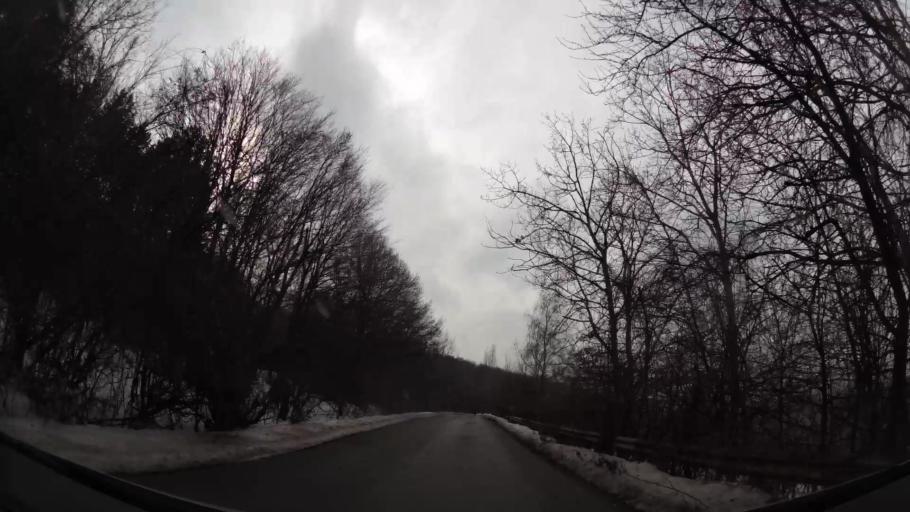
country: BG
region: Sofiya
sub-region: Obshtina Bozhurishte
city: Bozhurishte
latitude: 42.6589
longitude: 23.2049
